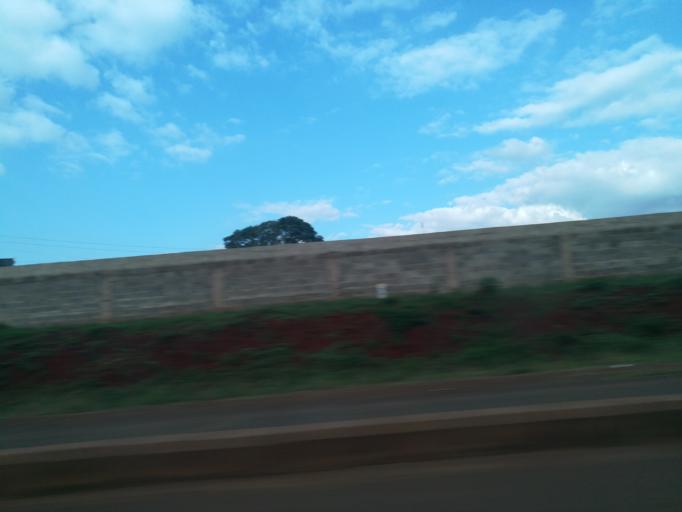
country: KE
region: Nairobi Area
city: Thika
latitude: -1.0345
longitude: 37.0650
